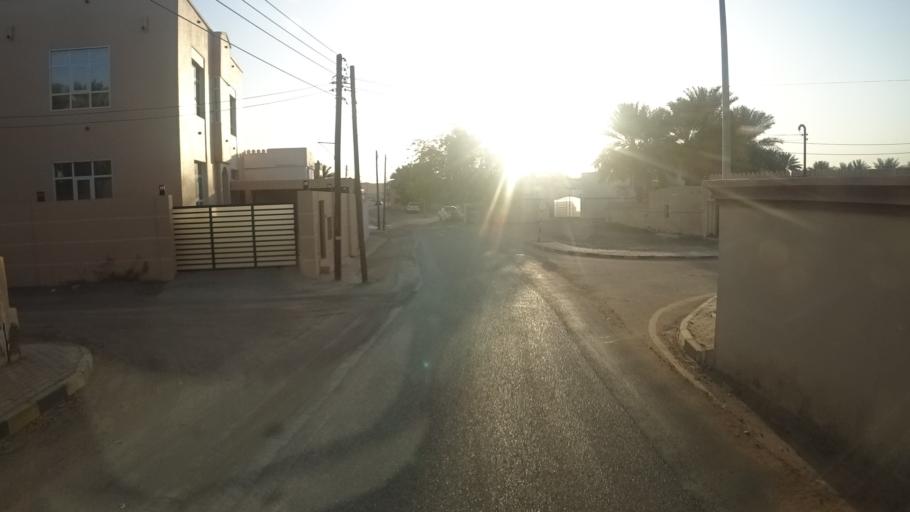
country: OM
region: Ash Sharqiyah
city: Badiyah
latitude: 22.4999
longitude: 58.7424
